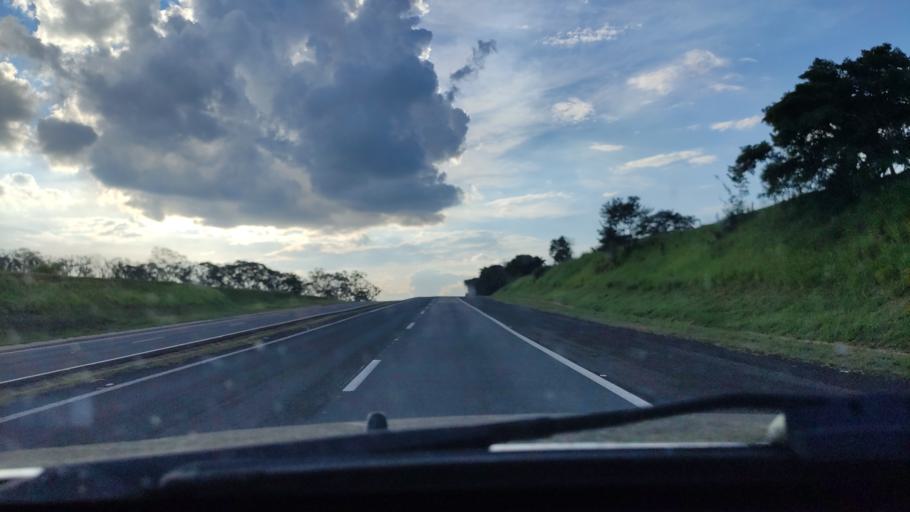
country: BR
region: Sao Paulo
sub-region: Maracai
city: Maracai
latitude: -22.4965
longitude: -50.9030
